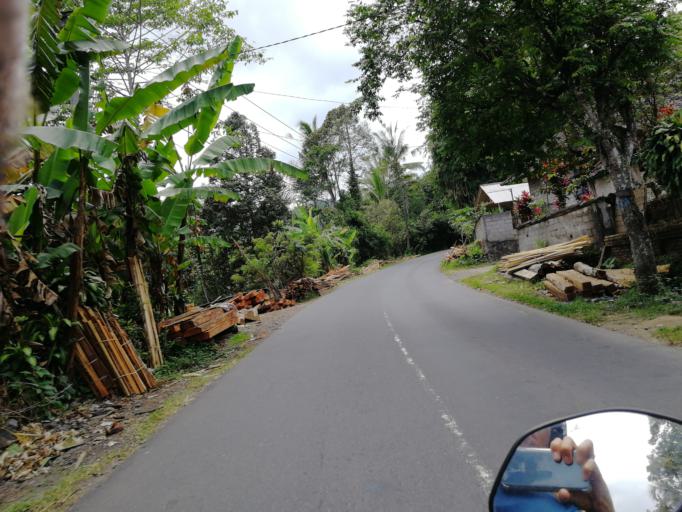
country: ID
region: Bali
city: Banjar Wates Tengah
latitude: -8.4531
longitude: 115.4564
